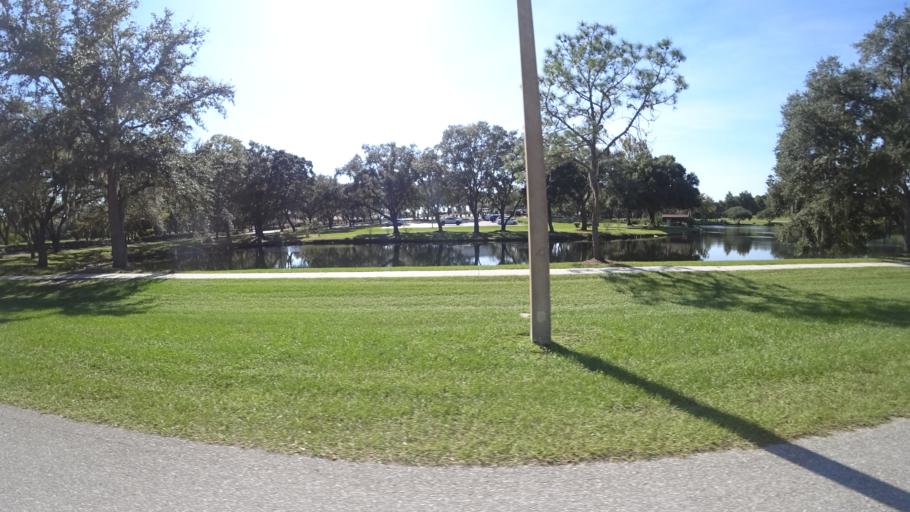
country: US
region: Florida
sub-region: Sarasota County
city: The Meadows
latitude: 27.4239
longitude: -82.4334
